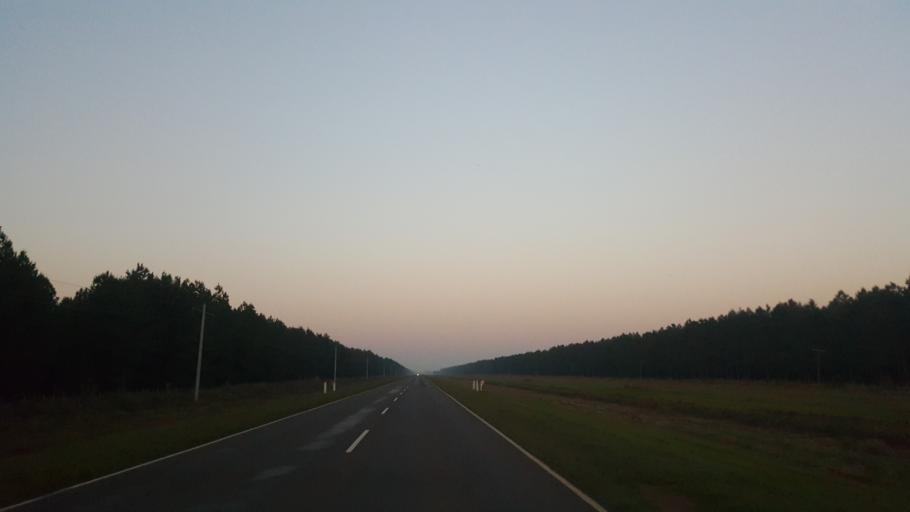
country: PY
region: Itapua
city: San Cosme y Damian
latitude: -27.5827
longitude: -56.2979
